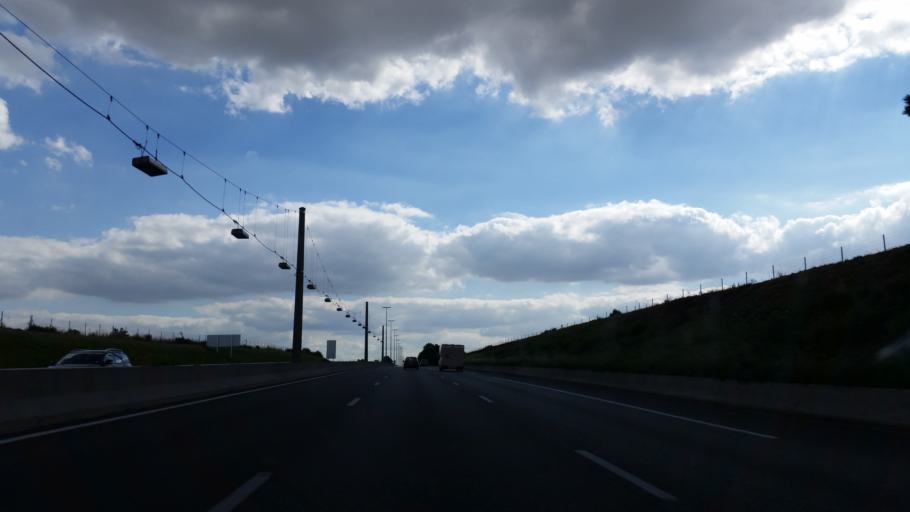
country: FR
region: Nord-Pas-de-Calais
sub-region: Departement du Pas-de-Calais
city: Fampoux
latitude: 50.2857
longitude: 2.8786
